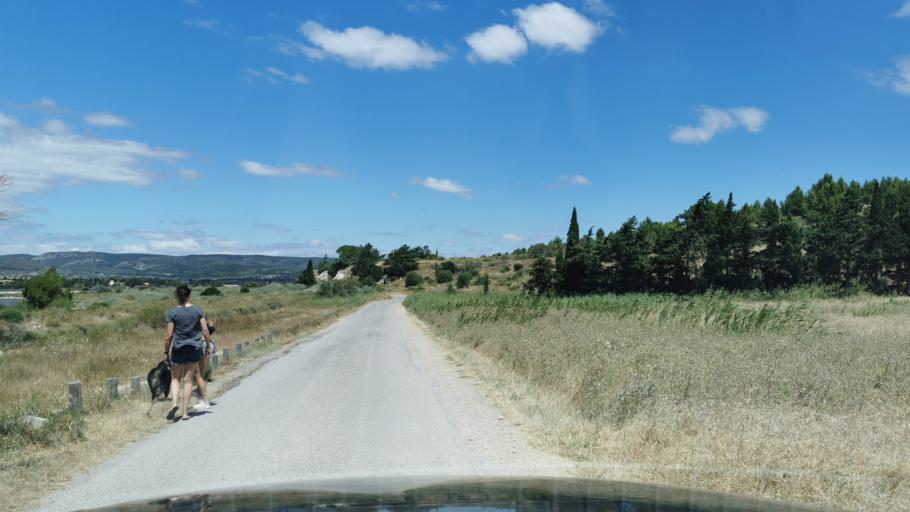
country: FR
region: Languedoc-Roussillon
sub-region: Departement de l'Aude
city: Peyriac-de-Mer
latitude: 43.0844
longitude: 2.9695
